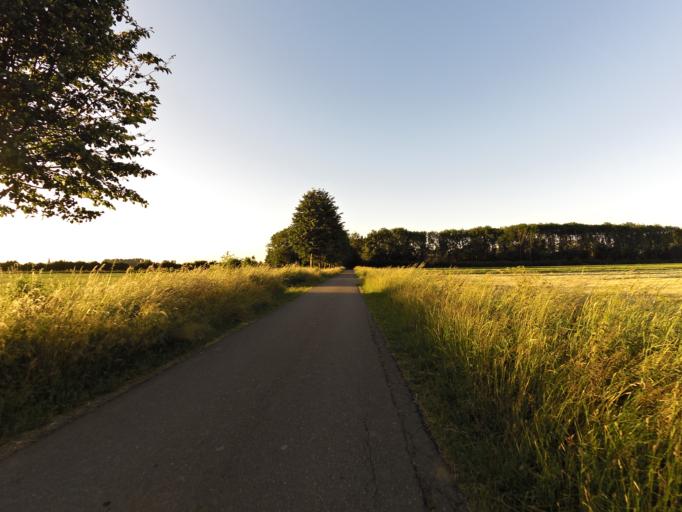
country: NL
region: Gelderland
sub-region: Gemeente Doesburg
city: Doesburg
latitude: 51.9946
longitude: 6.1690
